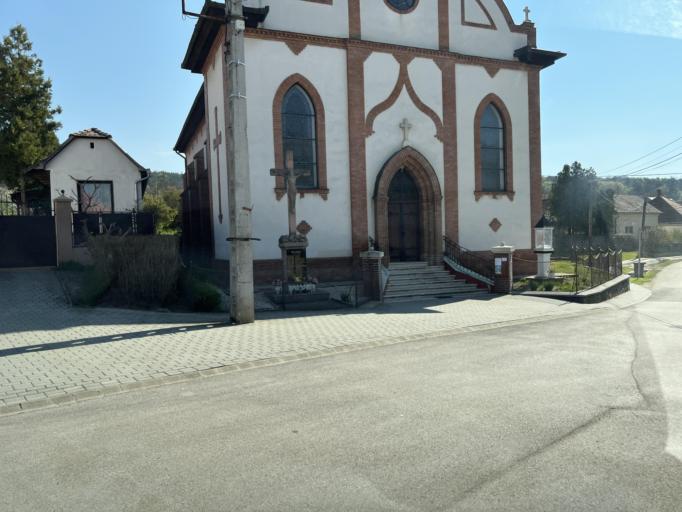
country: HU
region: Pest
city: Orbottyan
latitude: 47.7409
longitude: 19.3152
